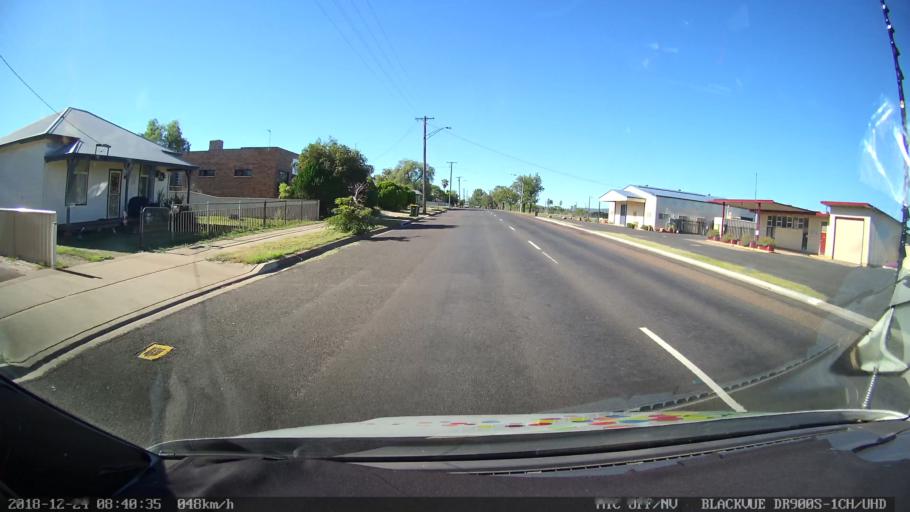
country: AU
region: New South Wales
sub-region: Liverpool Plains
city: Quirindi
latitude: -31.3560
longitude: 150.6463
